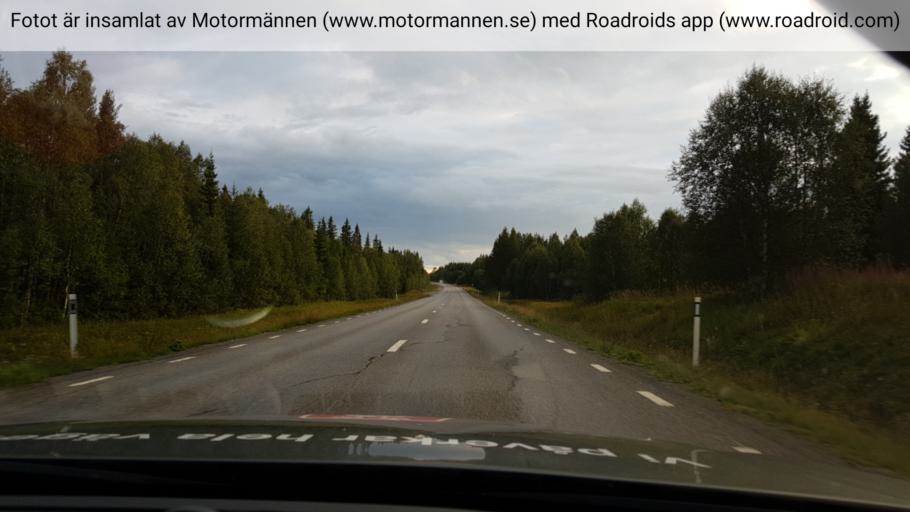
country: SE
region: Jaemtland
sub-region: OEstersunds Kommun
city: Lit
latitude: 63.4510
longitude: 15.1592
